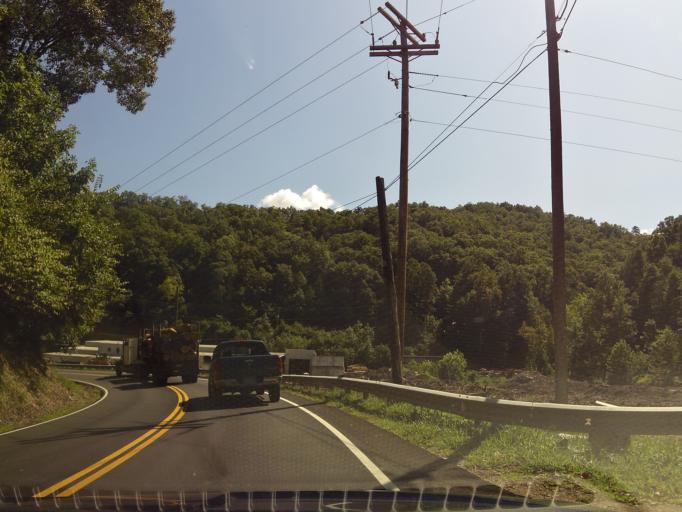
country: US
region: Kentucky
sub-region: Leslie County
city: Hyden
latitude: 37.1475
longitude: -83.4057
